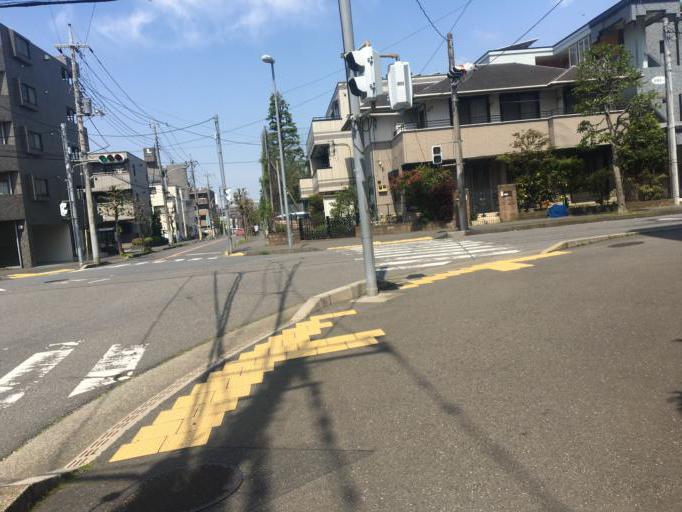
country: JP
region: Saitama
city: Wako
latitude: 35.7839
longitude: 139.6194
